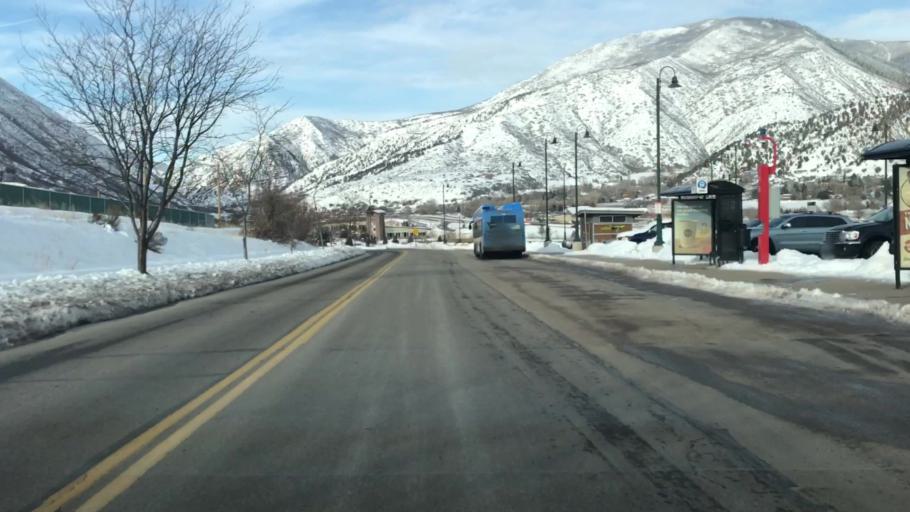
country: US
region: Colorado
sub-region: Garfield County
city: Glenwood Springs
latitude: 39.5577
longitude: -107.3536
